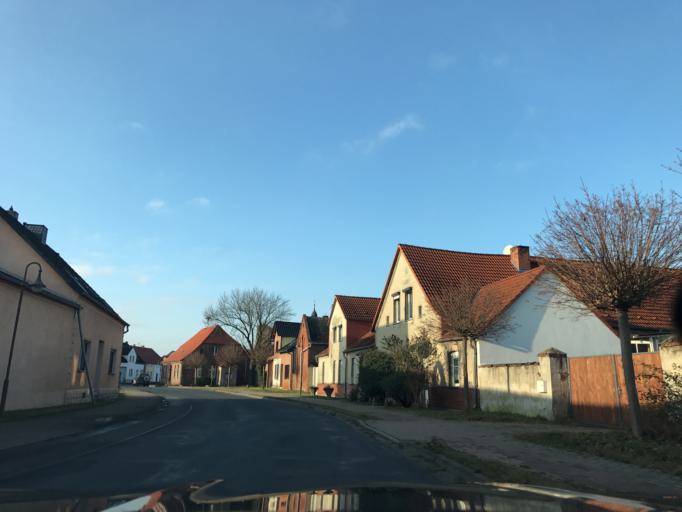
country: DE
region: Brandenburg
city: Graben
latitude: 52.2768
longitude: 12.3811
